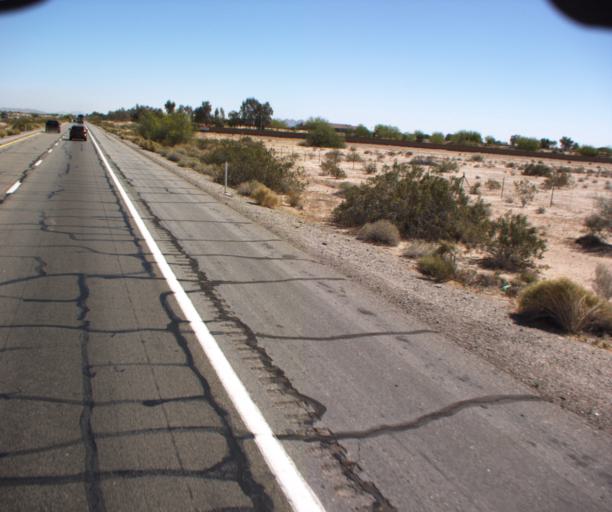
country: US
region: Arizona
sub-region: Yuma County
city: Wellton
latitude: 32.6513
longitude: -114.1862
